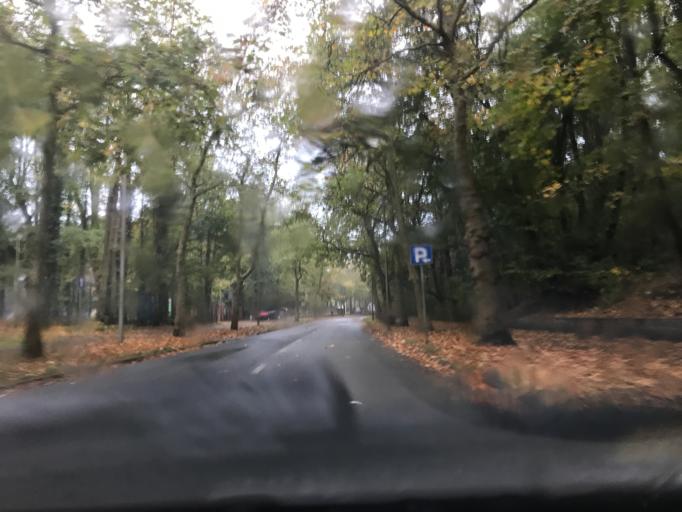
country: PL
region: West Pomeranian Voivodeship
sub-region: Swinoujscie
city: Swinoujscie
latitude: 53.9184
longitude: 14.2413
